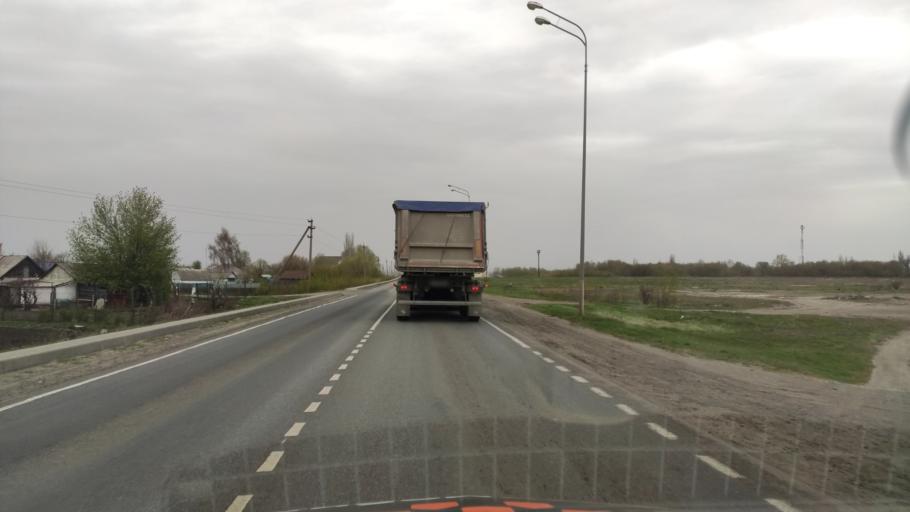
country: RU
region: Kursk
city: Gorshechnoye
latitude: 51.5283
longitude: 38.0228
